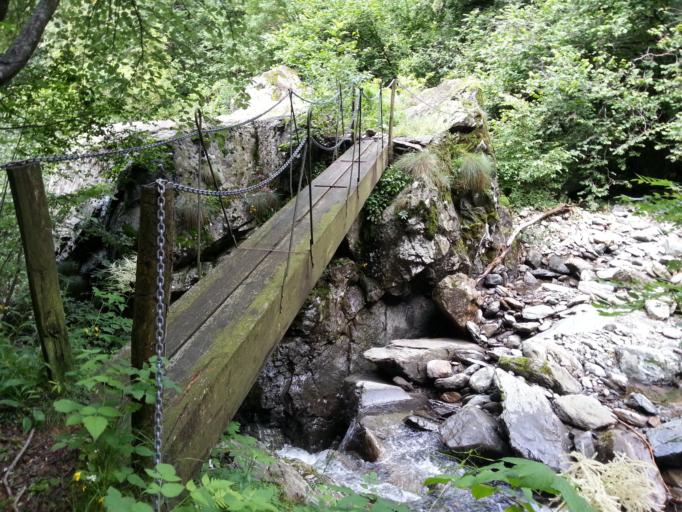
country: IT
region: Lombardy
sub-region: Provincia di Lecco
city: Pagnona
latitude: 46.0679
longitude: 9.4124
